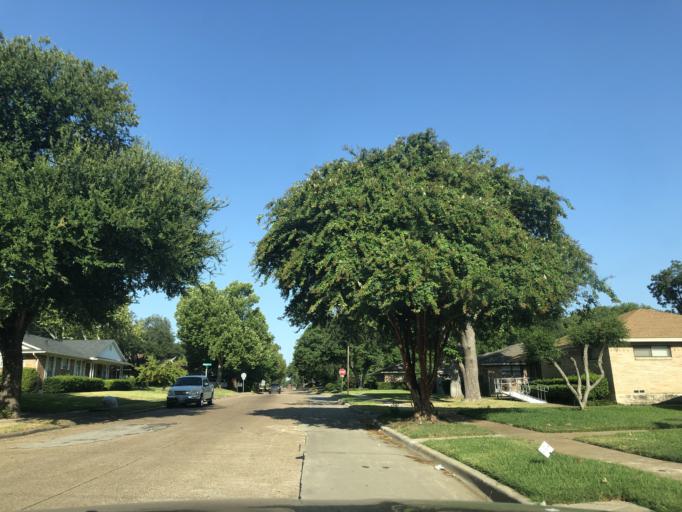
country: US
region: Texas
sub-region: Dallas County
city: Garland
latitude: 32.8710
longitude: -96.6425
